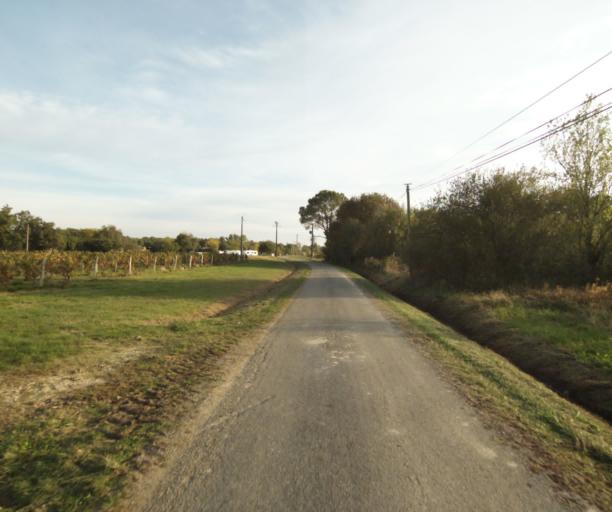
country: FR
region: Midi-Pyrenees
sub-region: Departement du Tarn-et-Garonne
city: Campsas
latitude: 43.9060
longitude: 1.3399
